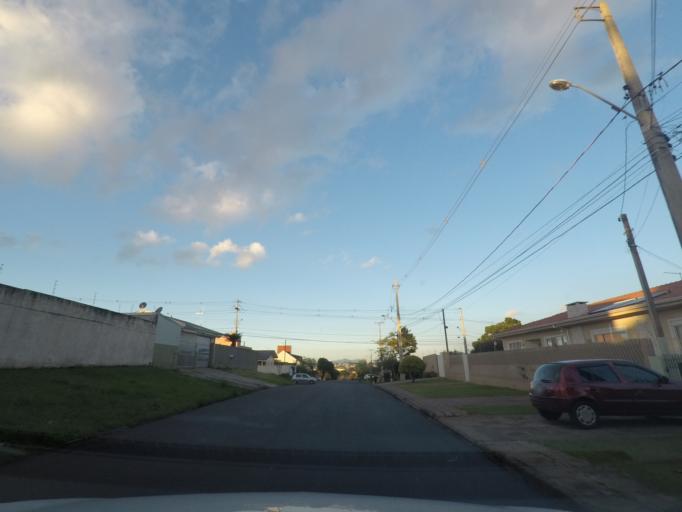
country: BR
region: Parana
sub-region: Sao Jose Dos Pinhais
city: Sao Jose dos Pinhais
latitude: -25.4942
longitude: -49.2584
